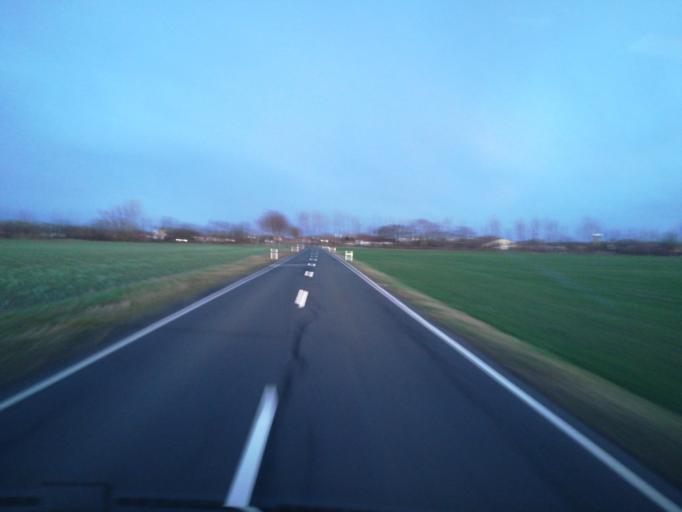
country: DE
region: Saxony
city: Delitzsch
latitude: 51.5362
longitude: 12.3024
